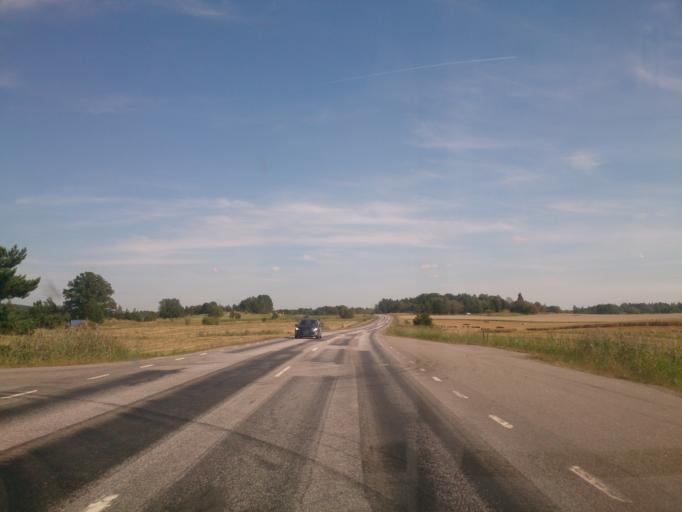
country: SE
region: OEstergoetland
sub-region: Norrkopings Kommun
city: Norrkoping
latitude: 58.4913
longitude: 16.1544
